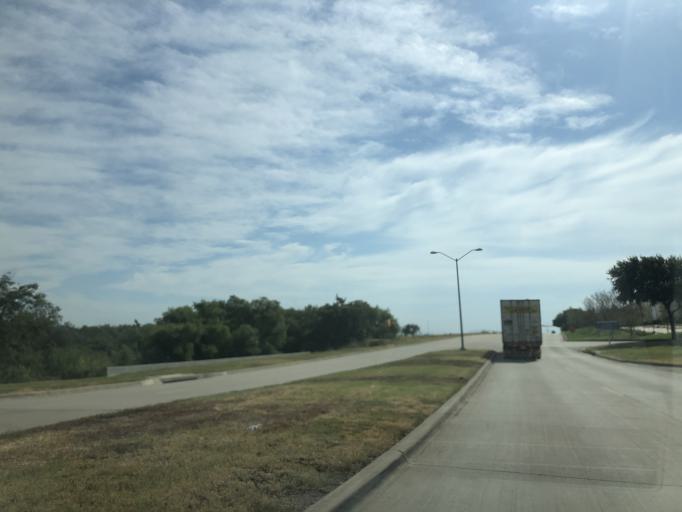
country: US
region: Texas
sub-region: Tarrant County
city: Haslet
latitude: 32.9739
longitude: -97.3330
